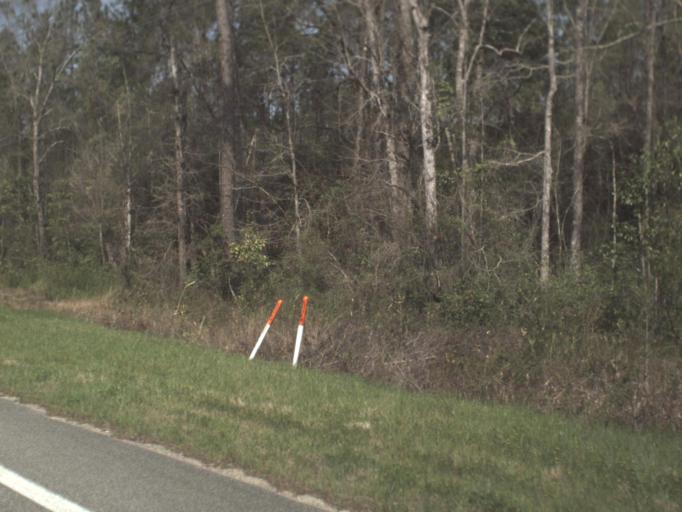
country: US
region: Florida
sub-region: Liberty County
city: Bristol
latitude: 30.3874
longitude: -84.7752
